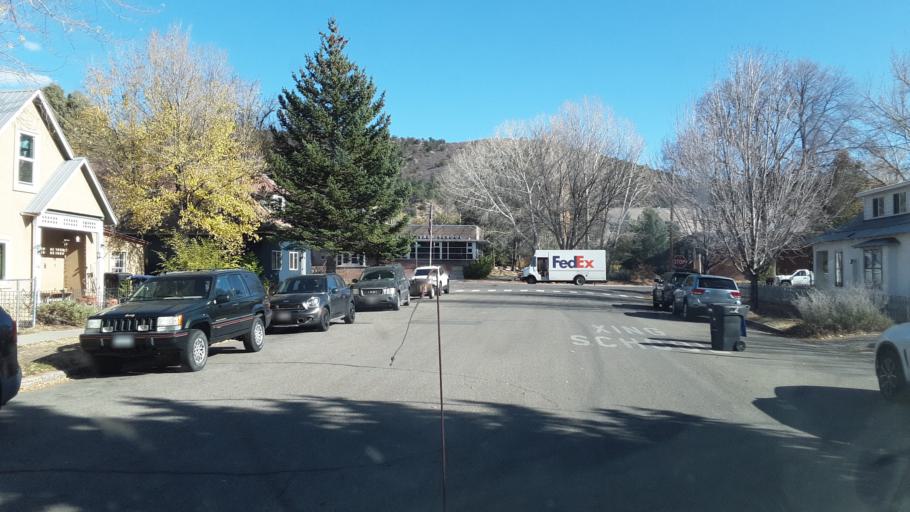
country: US
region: Colorado
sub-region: La Plata County
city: Durango
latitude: 37.2678
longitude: -107.8759
